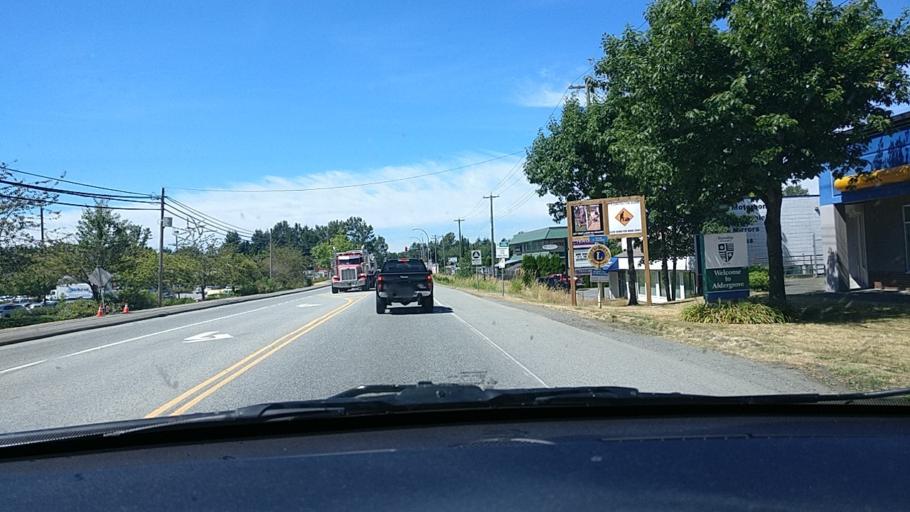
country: CA
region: British Columbia
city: Aldergrove
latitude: 49.0577
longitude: -122.4599
